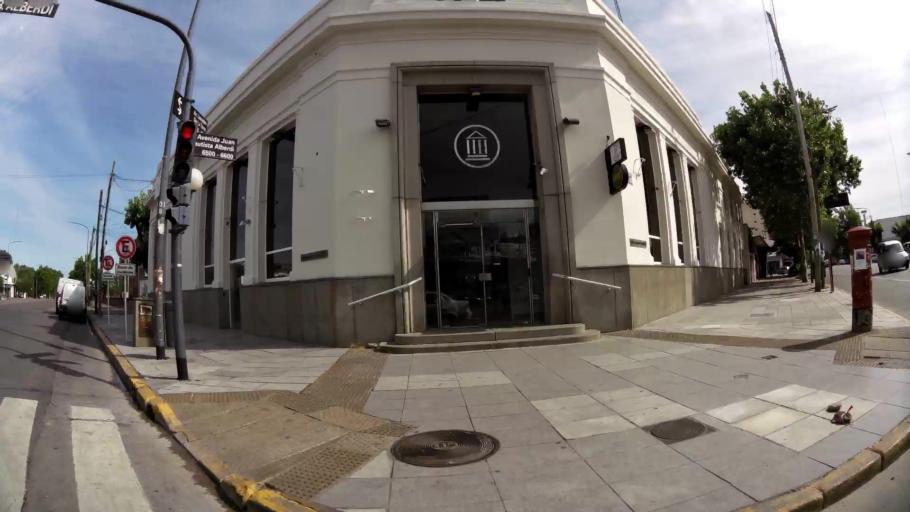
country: AR
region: Buenos Aires F.D.
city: Villa Lugano
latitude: -34.6563
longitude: -58.5080
